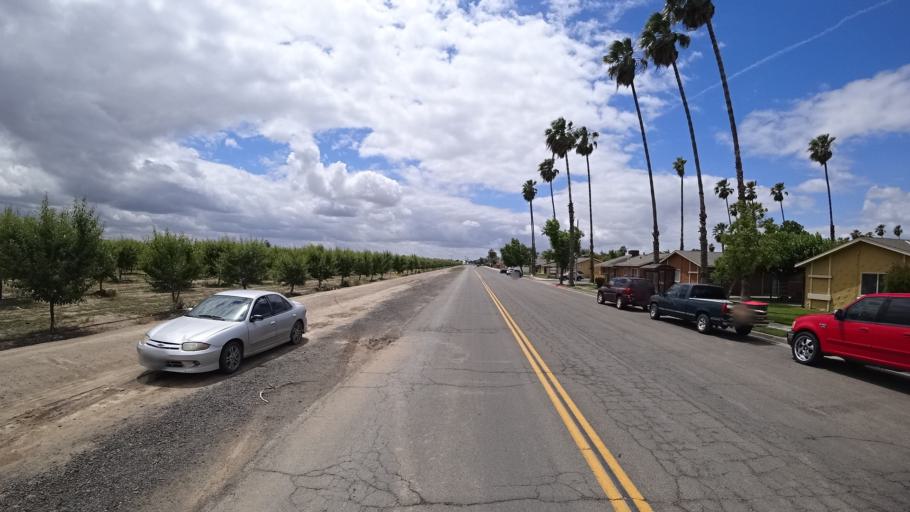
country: US
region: California
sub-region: Kings County
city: Hanford
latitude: 36.3388
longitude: -119.6236
